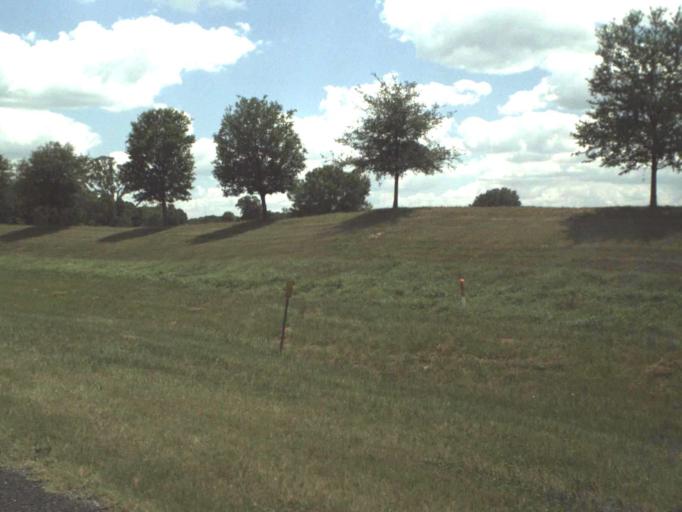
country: US
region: Florida
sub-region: Marion County
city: Ocala
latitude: 29.2725
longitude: -82.1521
